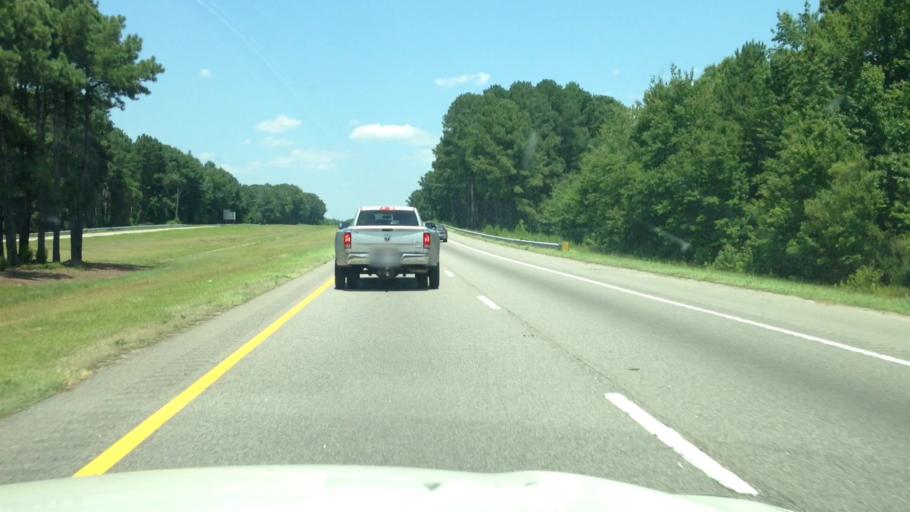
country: US
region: North Carolina
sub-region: Robeson County
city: Fairmont
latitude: 34.5583
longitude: -79.1839
